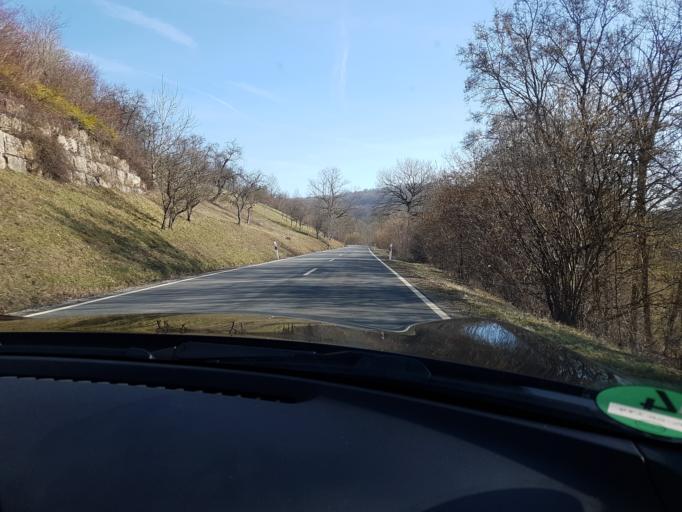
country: DE
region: Baden-Wuerttemberg
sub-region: Regierungsbezirk Stuttgart
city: Krautheim
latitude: 49.3770
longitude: 9.6462
